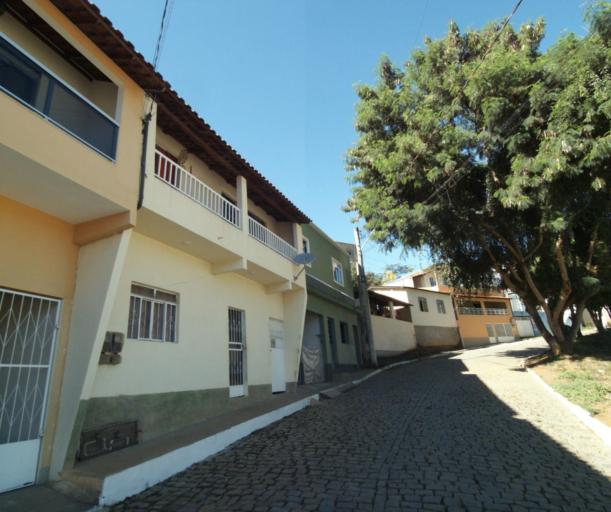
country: BR
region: Minas Gerais
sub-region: Espera Feliz
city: Espera Feliz
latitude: -20.6916
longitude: -41.8466
